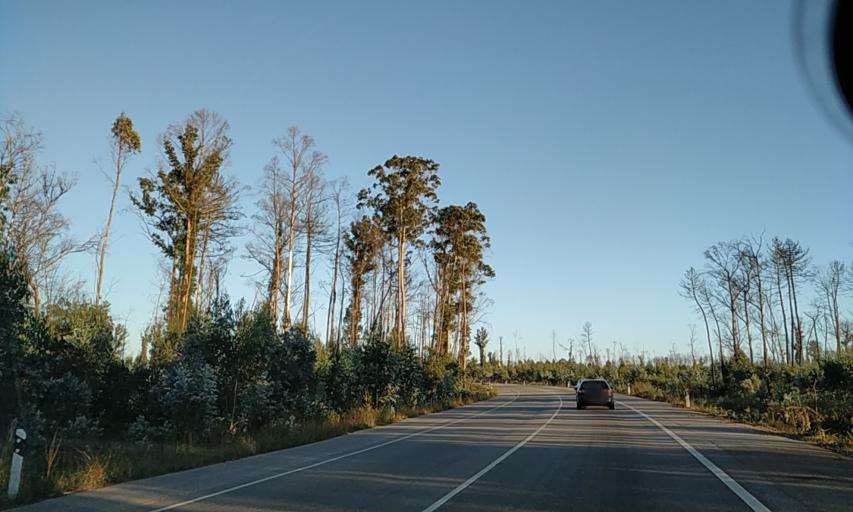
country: PT
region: Aveiro
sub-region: Oliveira do Bairro
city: Oia
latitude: 40.5609
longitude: -8.5632
